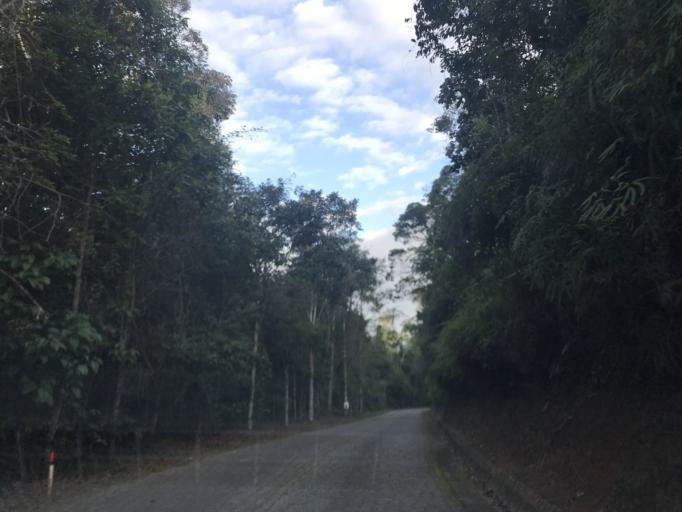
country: BR
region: Bahia
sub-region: Gandu
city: Gandu
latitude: -13.9045
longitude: -39.4609
